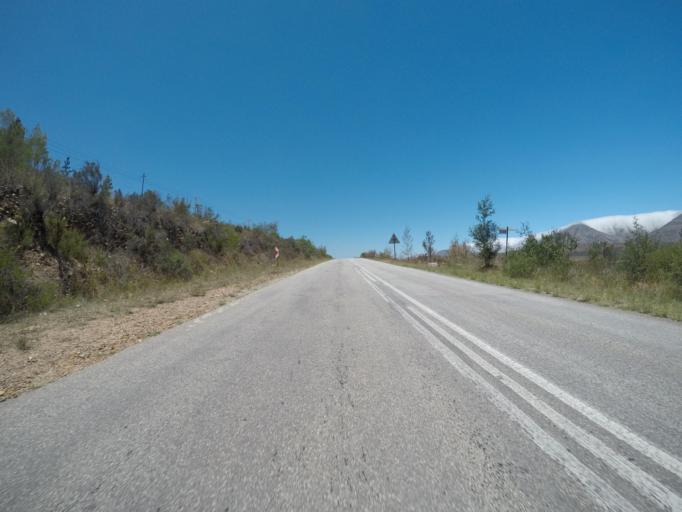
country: ZA
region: Eastern Cape
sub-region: Cacadu District Municipality
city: Kareedouw
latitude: -33.8309
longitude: 23.9008
